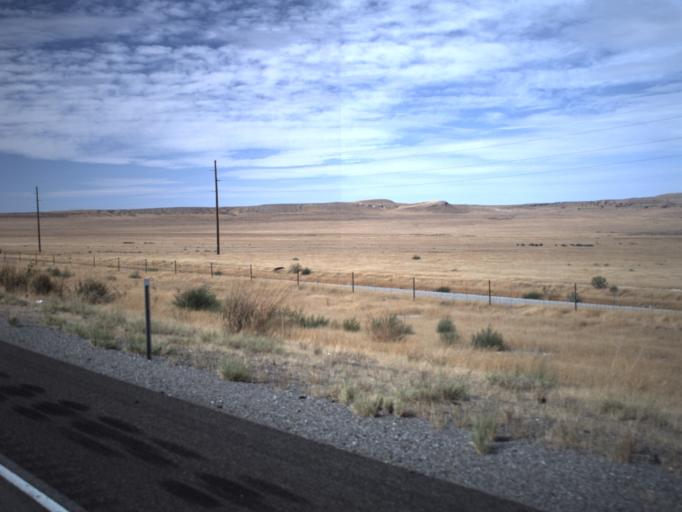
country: US
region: Utah
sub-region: Tooele County
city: Grantsville
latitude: 40.7909
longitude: -112.9553
